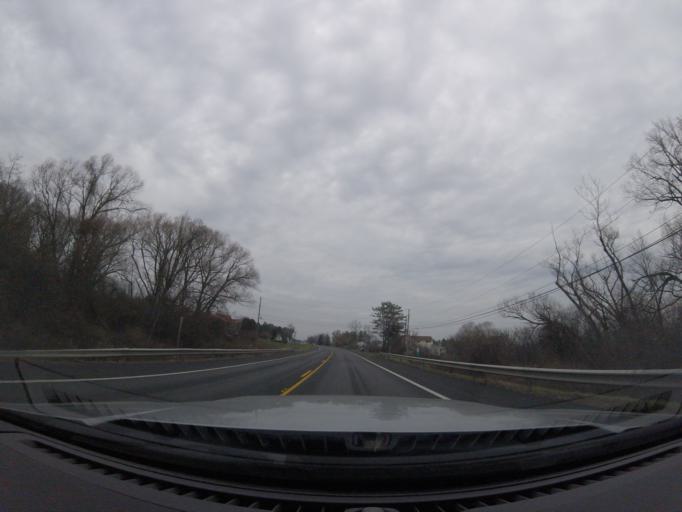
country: US
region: New York
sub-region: Schuyler County
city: Watkins Glen
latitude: 42.4481
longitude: -76.9084
